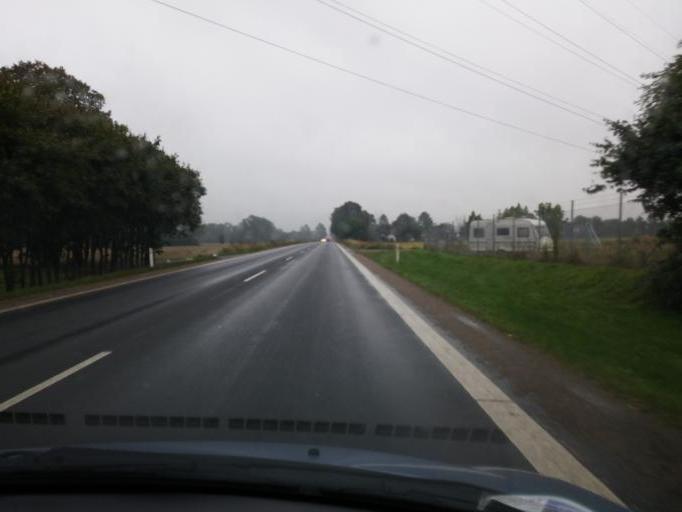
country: DK
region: South Denmark
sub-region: Odense Kommune
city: Bullerup
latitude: 55.3876
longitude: 10.4956
